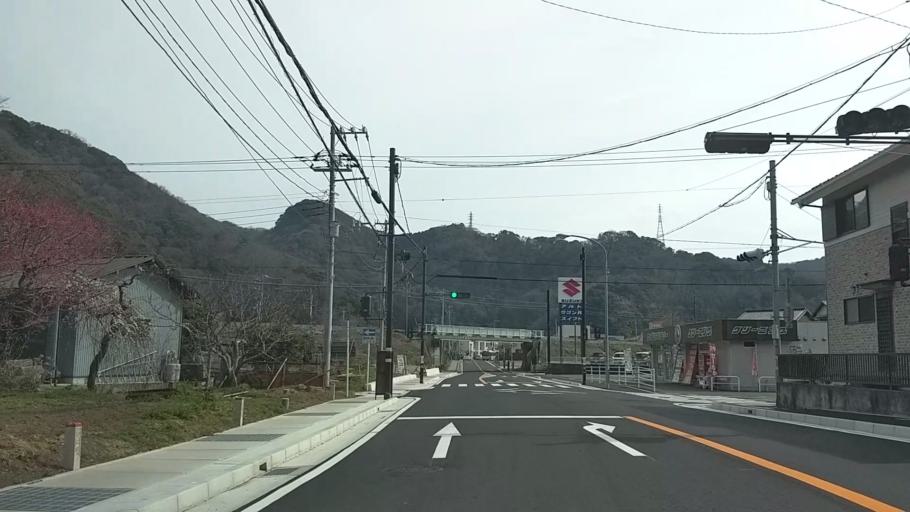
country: JP
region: Shizuoka
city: Shimoda
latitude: 34.6894
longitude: 138.9421
